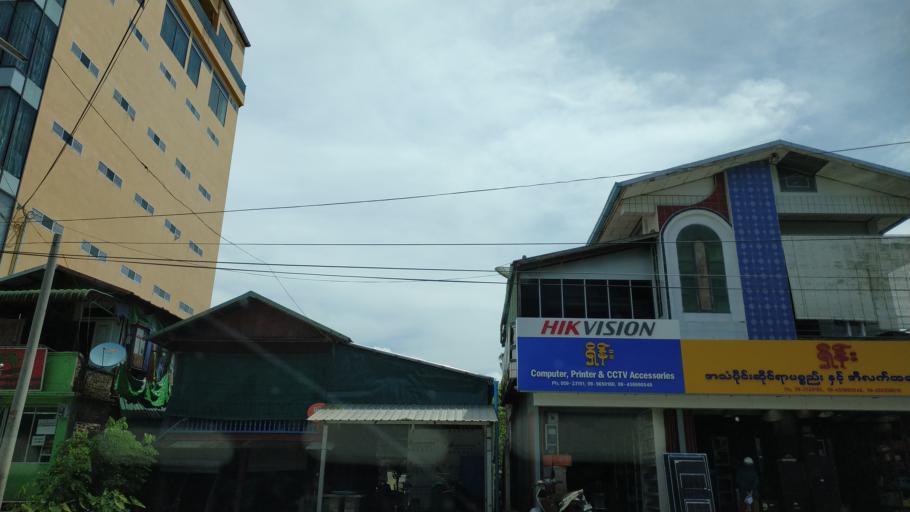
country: MM
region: Tanintharyi
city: Dawei
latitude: 14.0684
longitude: 98.1901
